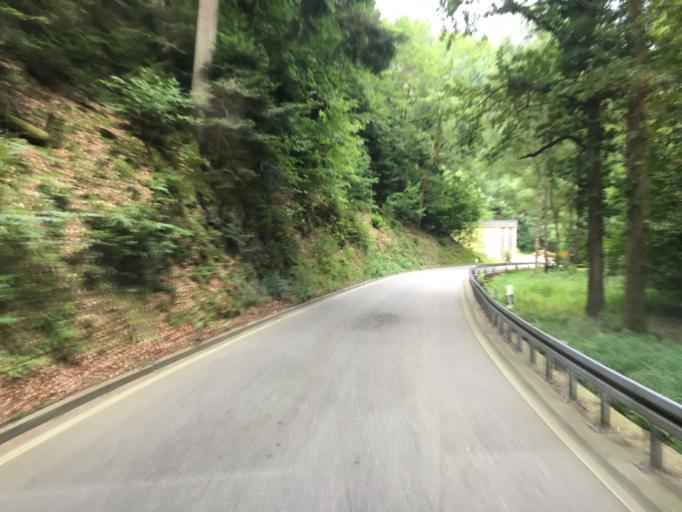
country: DE
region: Baden-Wuerttemberg
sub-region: Karlsruhe Region
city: Buhlertal
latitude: 48.7166
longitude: 8.2038
